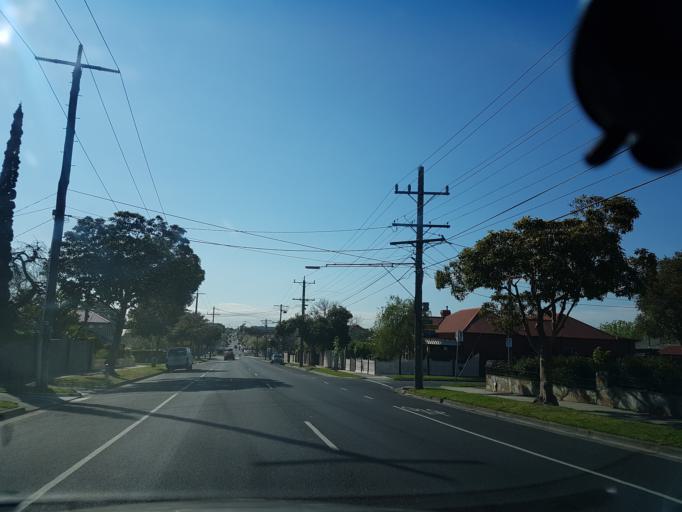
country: AU
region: Victoria
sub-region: Glen Eira
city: Bentleigh
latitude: -37.9103
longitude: 145.0318
